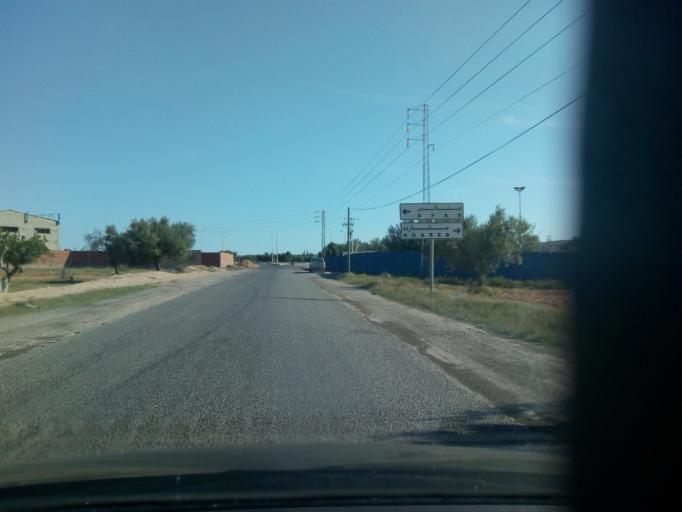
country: TN
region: Safaqis
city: Sfax
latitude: 34.7296
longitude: 10.6157
